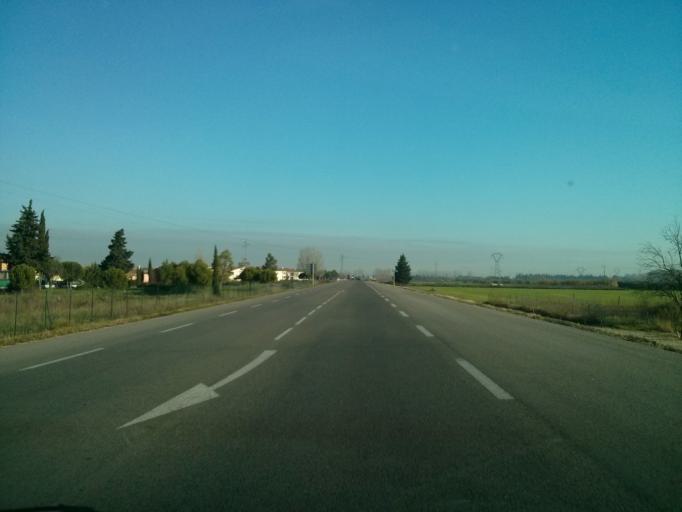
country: FR
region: Languedoc-Roussillon
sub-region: Departement du Gard
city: Milhaud
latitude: 43.7843
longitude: 4.3132
